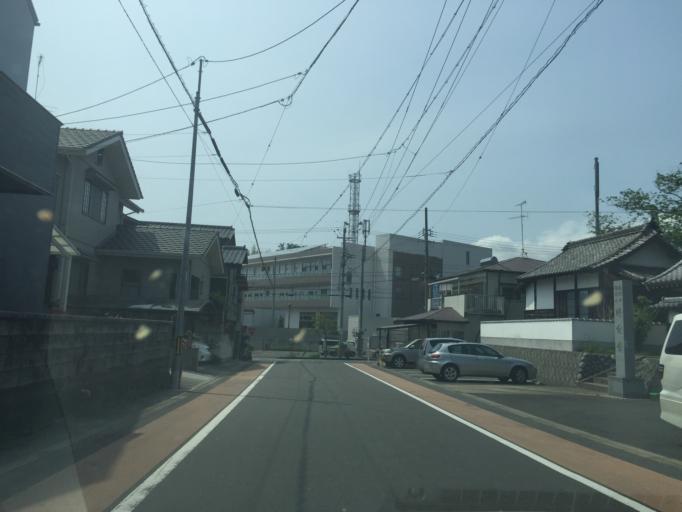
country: JP
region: Shizuoka
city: Kakegawa
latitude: 34.7775
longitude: 138.0201
